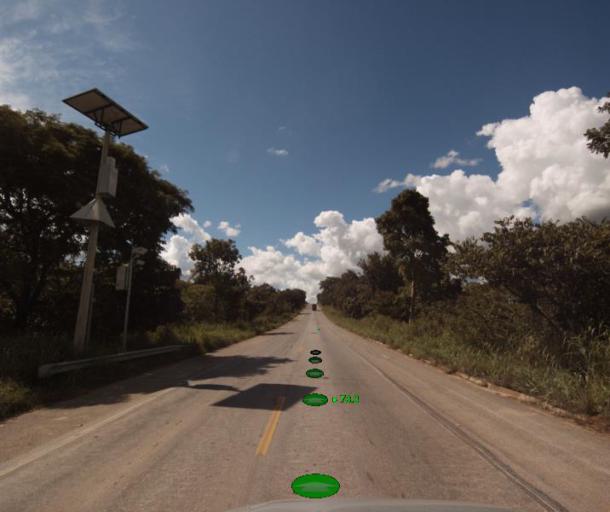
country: BR
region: Goias
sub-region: Porangatu
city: Porangatu
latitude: -13.4600
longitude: -49.1356
